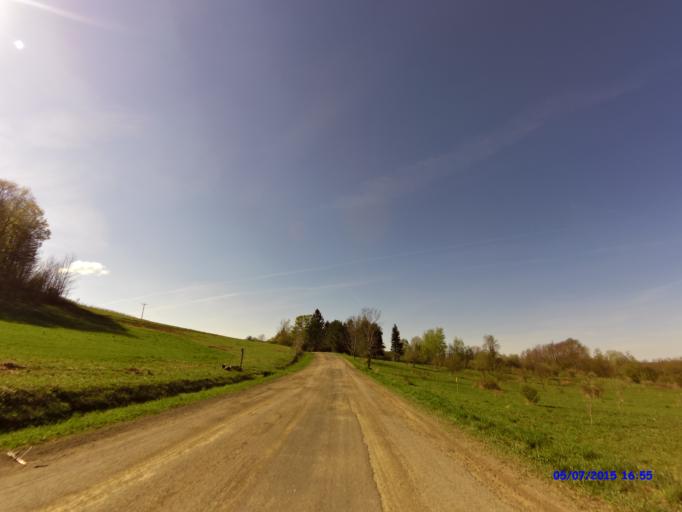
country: US
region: New York
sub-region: Cattaraugus County
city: Little Valley
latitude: 42.2997
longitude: -78.7492
